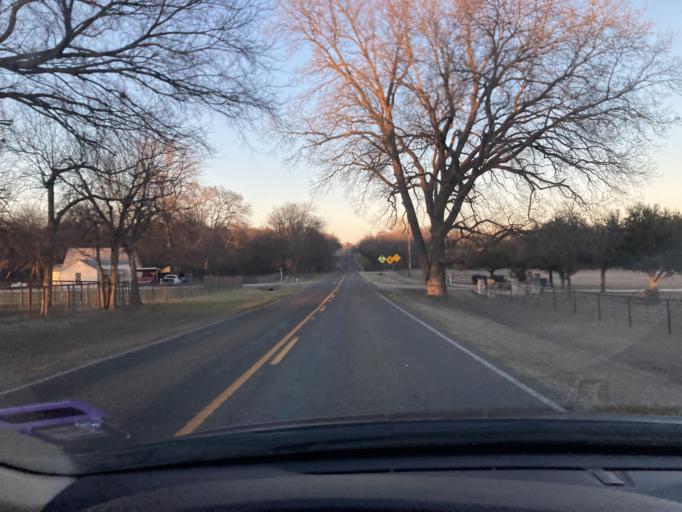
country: US
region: Texas
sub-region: Ellis County
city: Waxahachie
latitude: 32.3479
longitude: -96.8716
